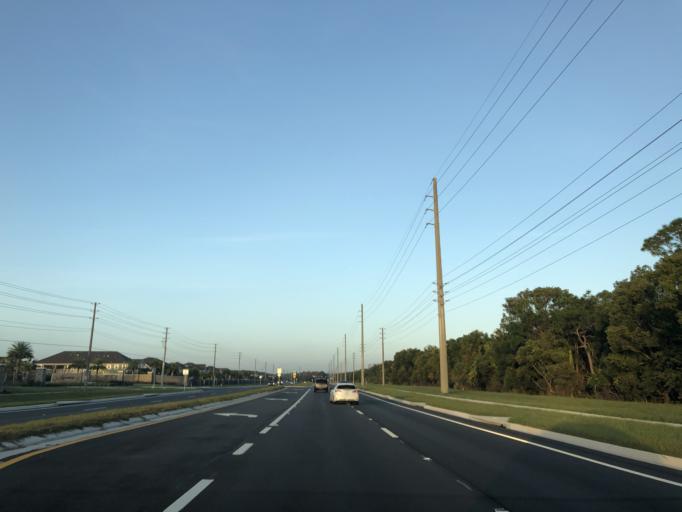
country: US
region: Florida
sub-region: Osceola County
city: Kissimmee
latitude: 28.3248
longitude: -81.4298
